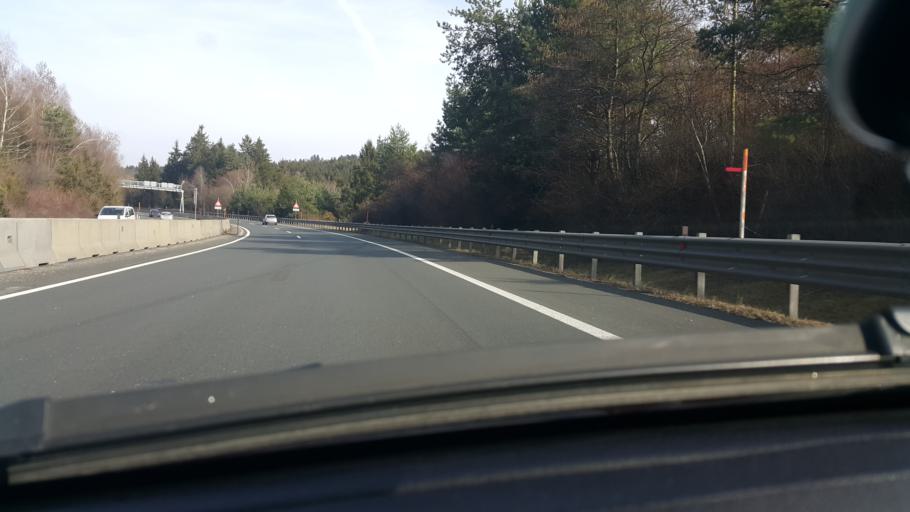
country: AT
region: Carinthia
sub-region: Politischer Bezirk Volkermarkt
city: Griffen
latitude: 46.7003
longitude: 14.7644
